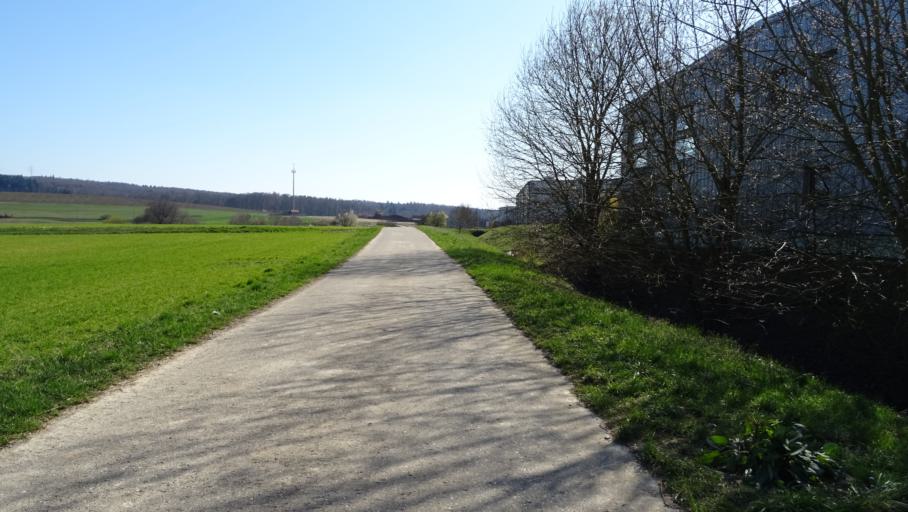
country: DE
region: Baden-Wuerttemberg
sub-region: Karlsruhe Region
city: Binau
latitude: 49.3470
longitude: 9.0458
